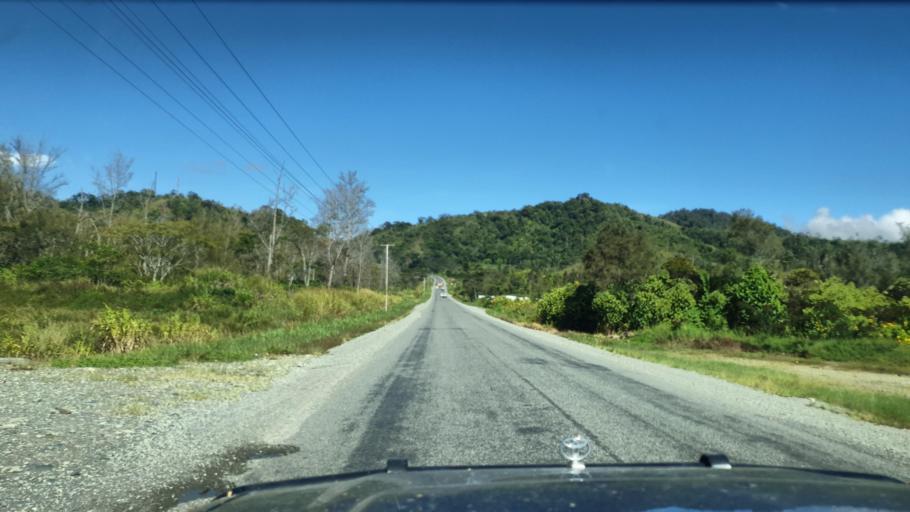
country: PG
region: Western Highlands
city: Rauna
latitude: -5.8246
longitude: 144.3833
